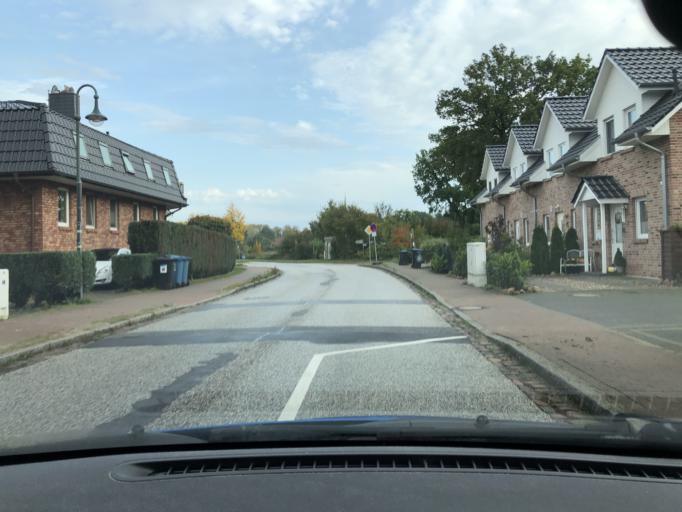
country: DE
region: Schleswig-Holstein
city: Siek
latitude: 53.6372
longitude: 10.2903
